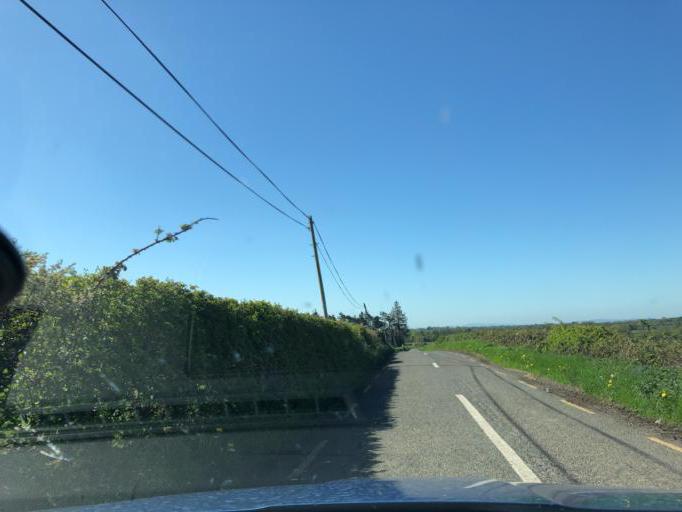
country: IE
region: Connaught
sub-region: County Galway
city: Portumna
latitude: 53.1900
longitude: -8.1629
